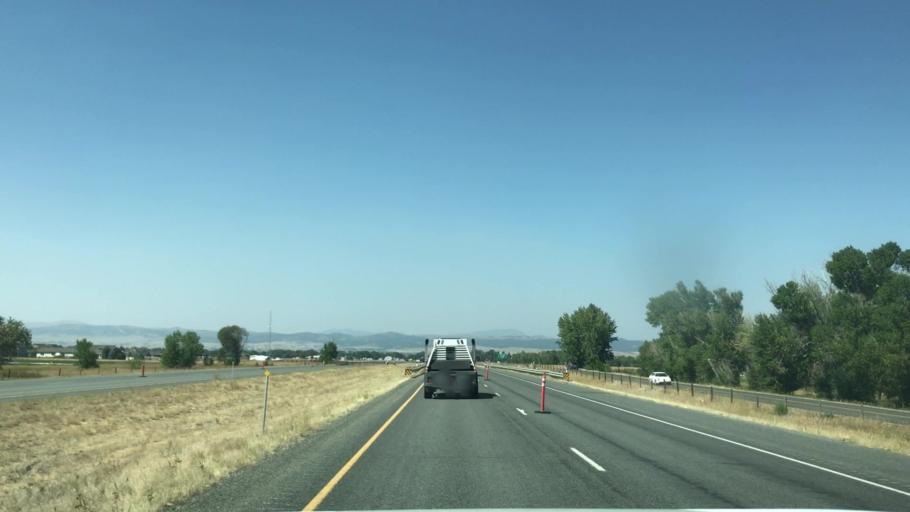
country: US
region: Montana
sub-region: Lewis and Clark County
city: Helena Valley West Central
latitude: 46.6462
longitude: -112.0112
